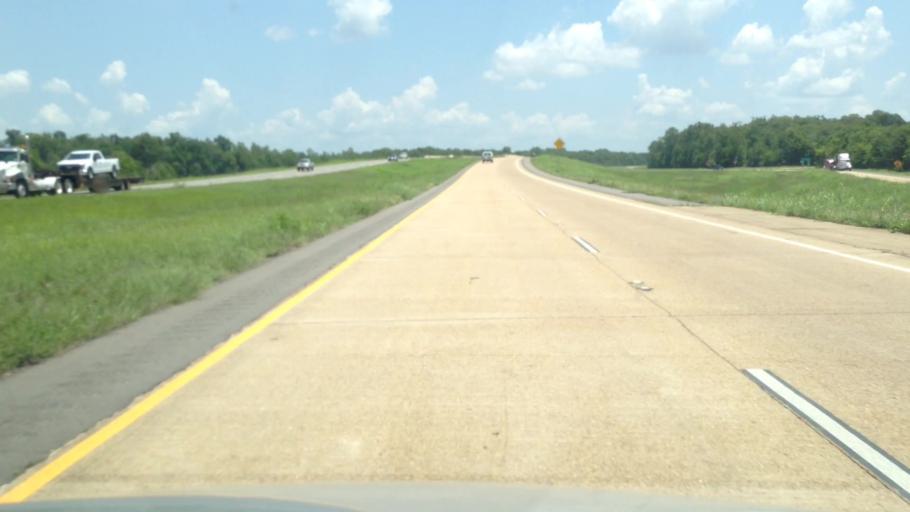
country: US
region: Louisiana
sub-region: Avoyelles Parish
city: Bunkie
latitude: 30.9891
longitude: -92.3119
